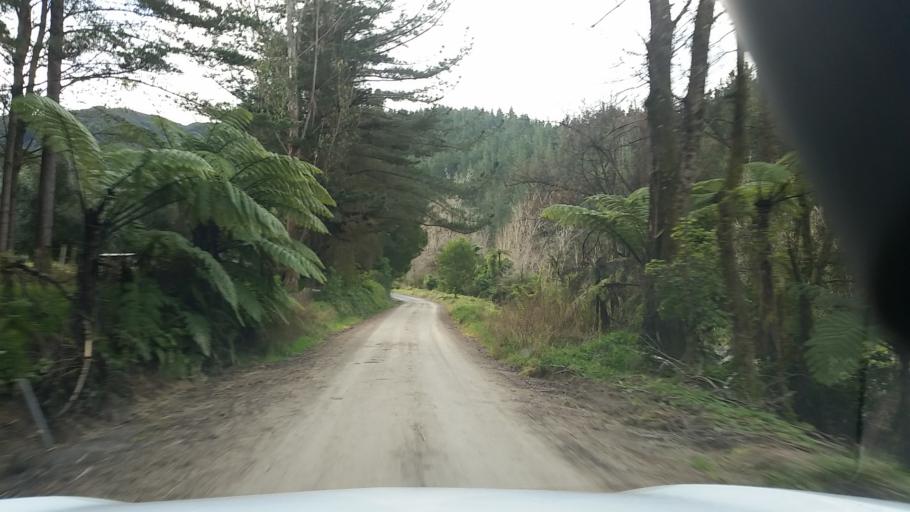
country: NZ
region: Taranaki
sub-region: South Taranaki District
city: Patea
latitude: -39.5759
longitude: 174.8243
